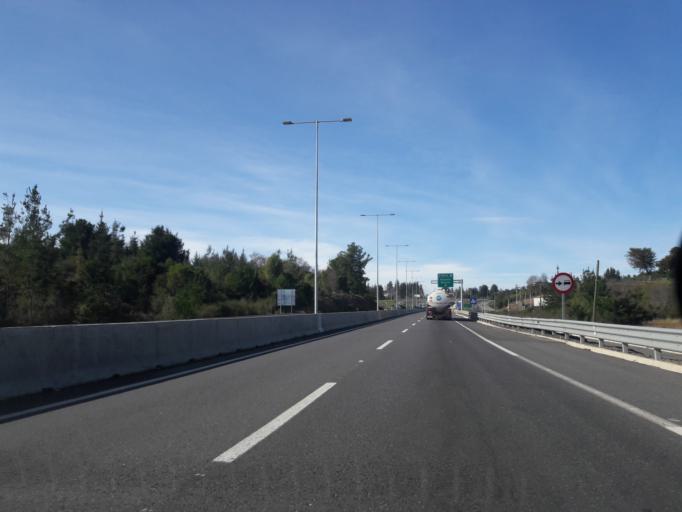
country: CL
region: Biobio
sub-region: Provincia de Biobio
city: Yumbel
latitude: -36.9609
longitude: -72.7253
